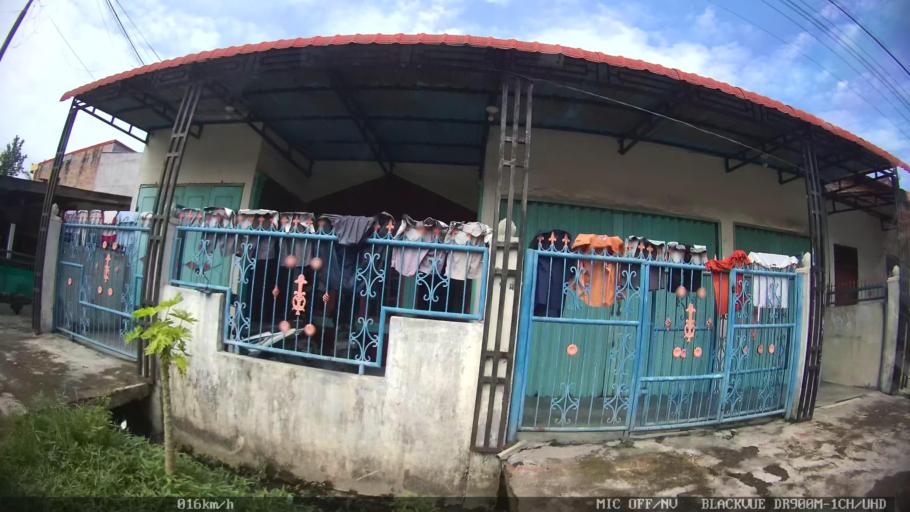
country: ID
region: North Sumatra
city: Medan
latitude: 3.5906
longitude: 98.7370
